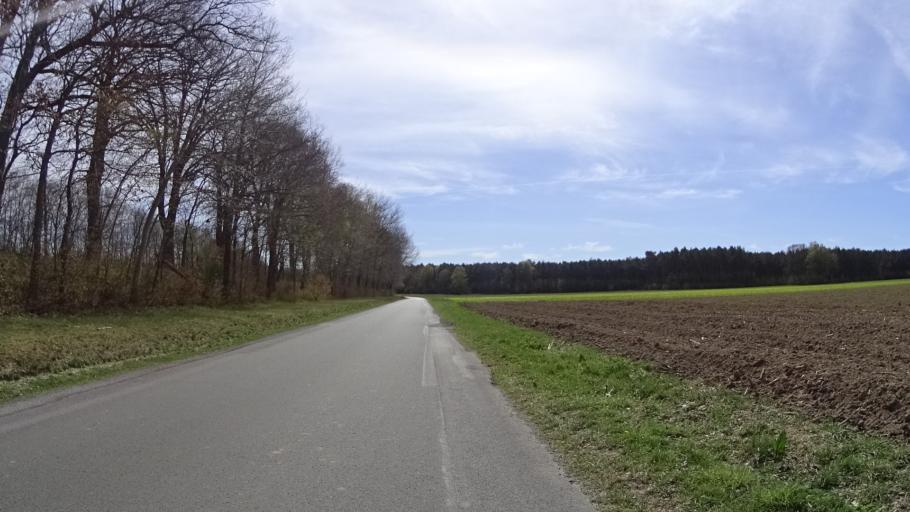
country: DE
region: Lower Saxony
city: Emsburen
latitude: 52.4229
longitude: 7.3558
